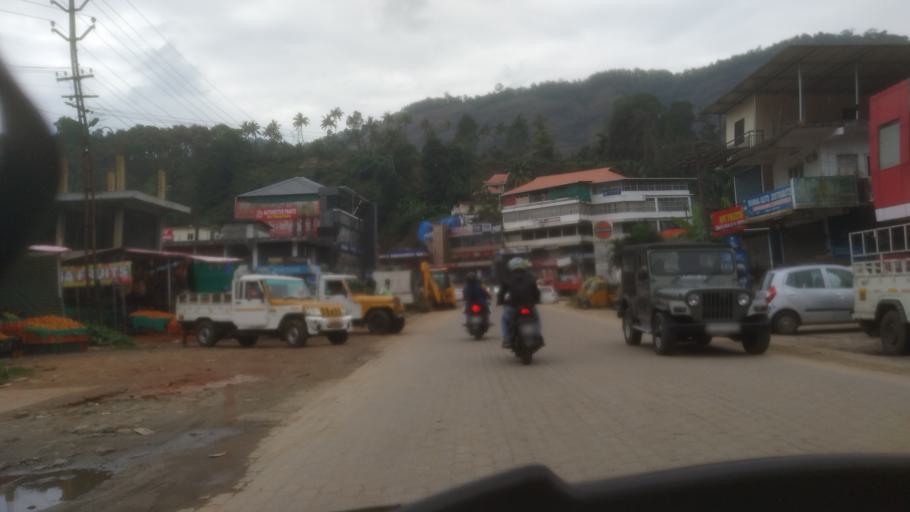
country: IN
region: Kerala
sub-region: Idukki
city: Munnar
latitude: 10.0094
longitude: 76.9580
